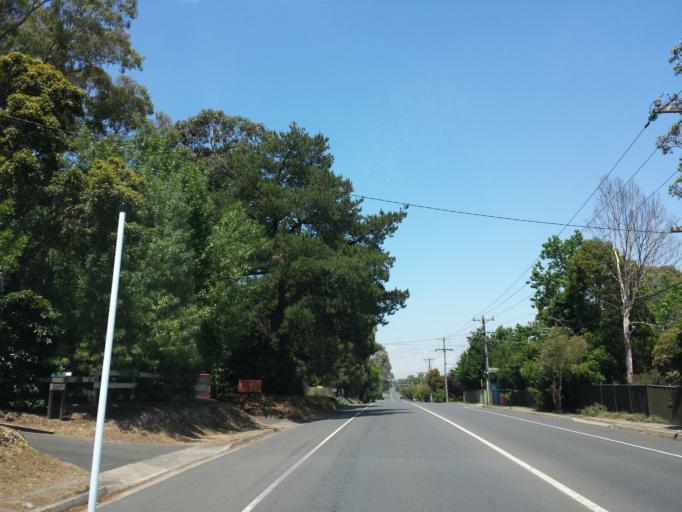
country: AU
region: Victoria
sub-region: Maroondah
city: Croydon North
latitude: -37.7900
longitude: 145.2918
